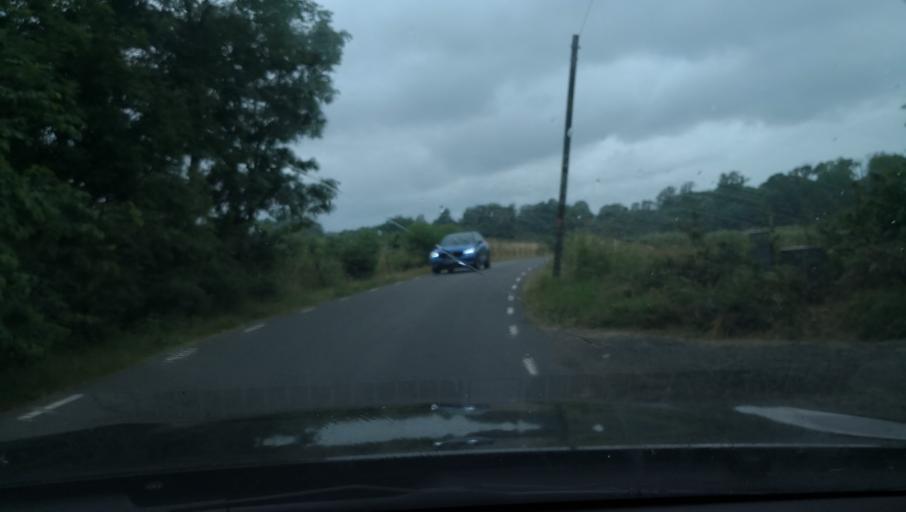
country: SE
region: Skane
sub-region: Simrishamns Kommun
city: Kivik
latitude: 55.6810
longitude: 14.2408
